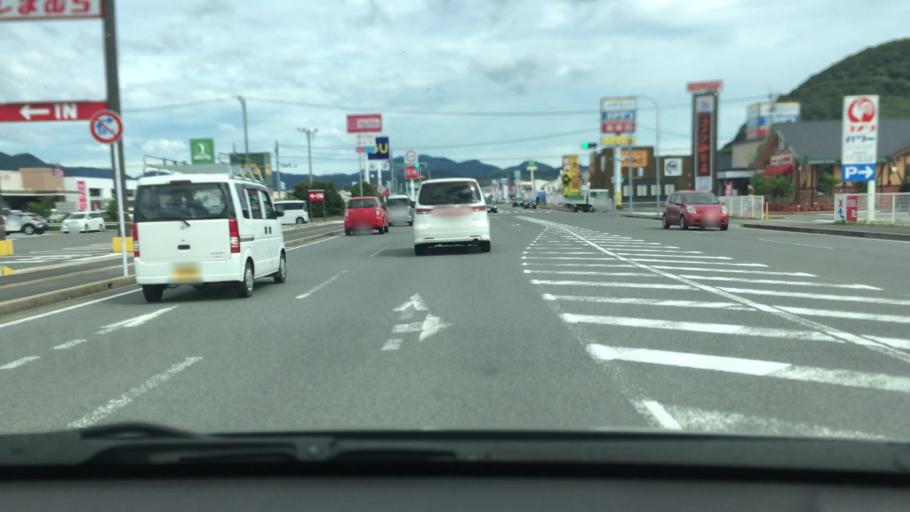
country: JP
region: Nagasaki
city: Togitsu
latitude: 32.8519
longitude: 129.8259
